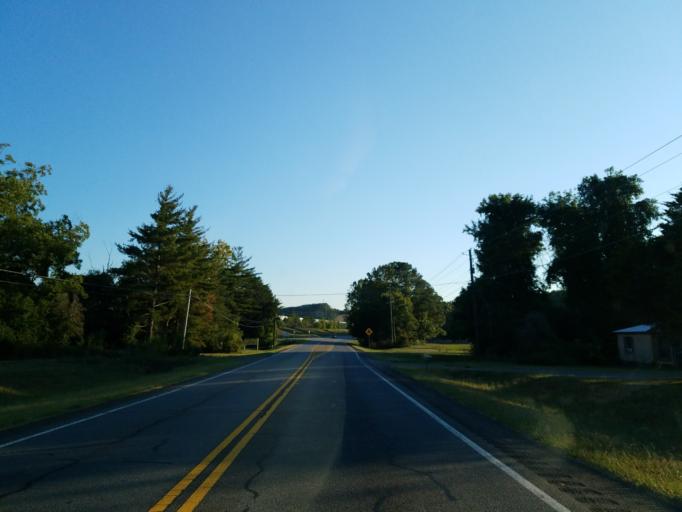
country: US
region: Georgia
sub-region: Bartow County
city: Rydal
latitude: 34.2978
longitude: -84.7323
